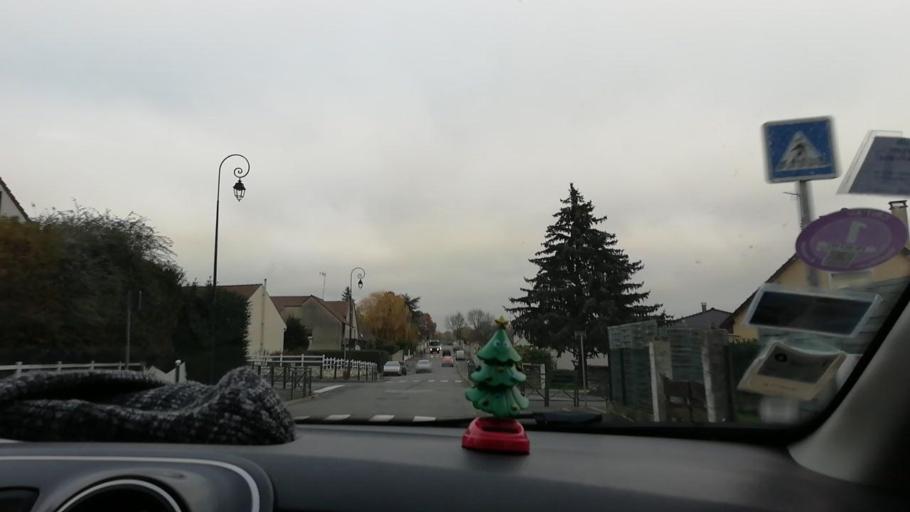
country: FR
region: Ile-de-France
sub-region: Departement de Seine-et-Marne
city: Monthyon
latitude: 49.0057
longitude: 2.8331
